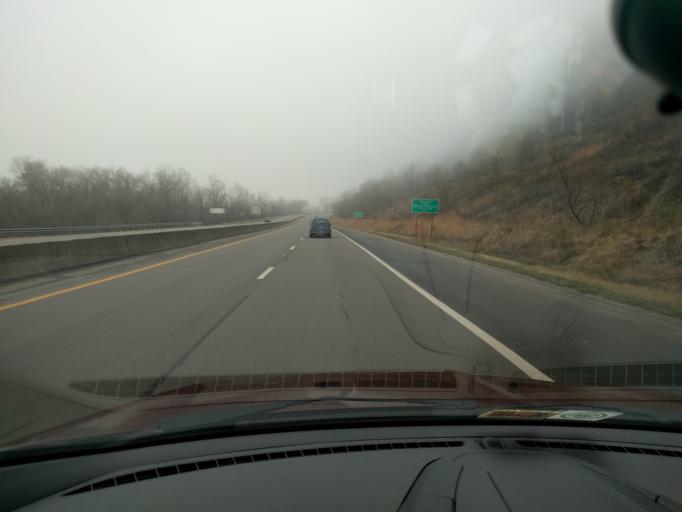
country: US
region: West Virginia
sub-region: Kanawha County
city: Chesapeake
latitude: 38.2121
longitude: -81.5118
